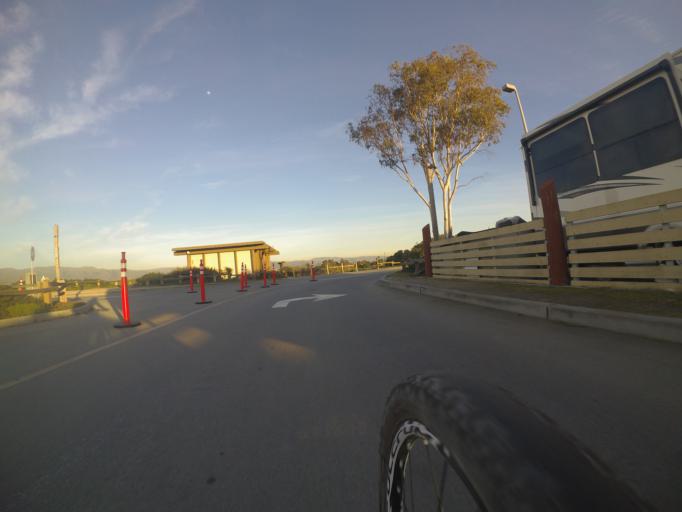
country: US
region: California
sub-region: Santa Clara County
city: Milpitas
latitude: 37.4297
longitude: -121.9796
